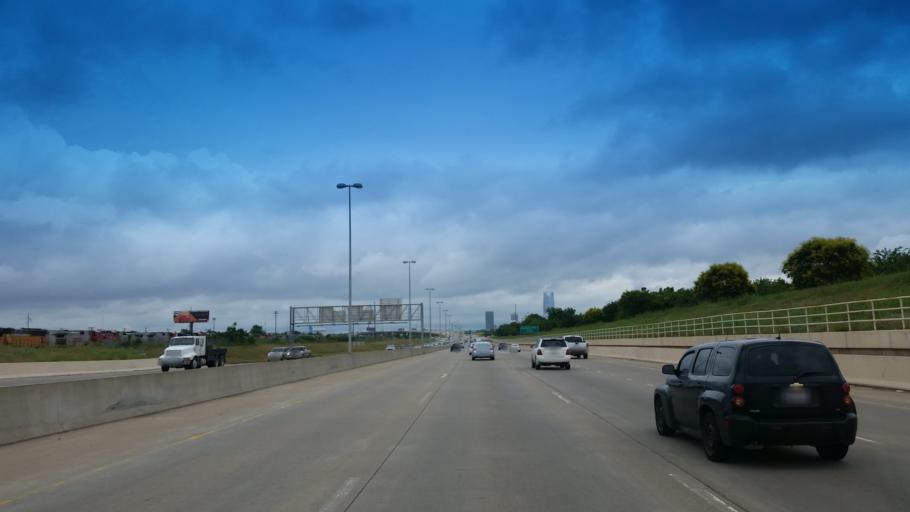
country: US
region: Oklahoma
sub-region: Oklahoma County
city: Oklahoma City
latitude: 35.5048
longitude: -97.5142
